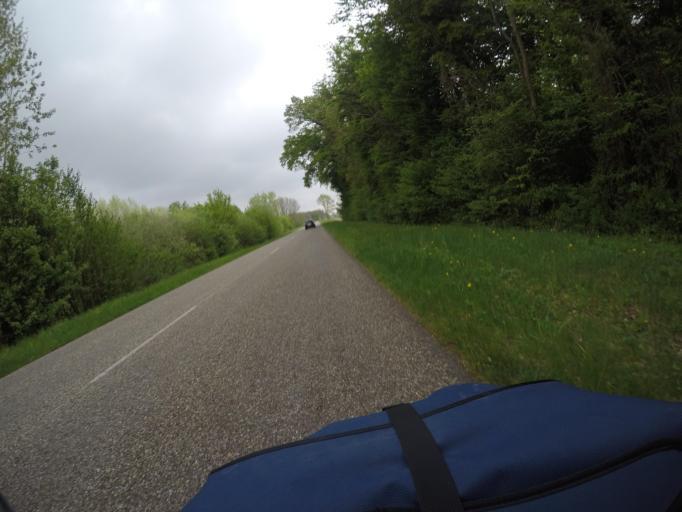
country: FR
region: Alsace
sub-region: Departement du Bas-Rhin
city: Drusenheim
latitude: 48.7854
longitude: 7.9758
